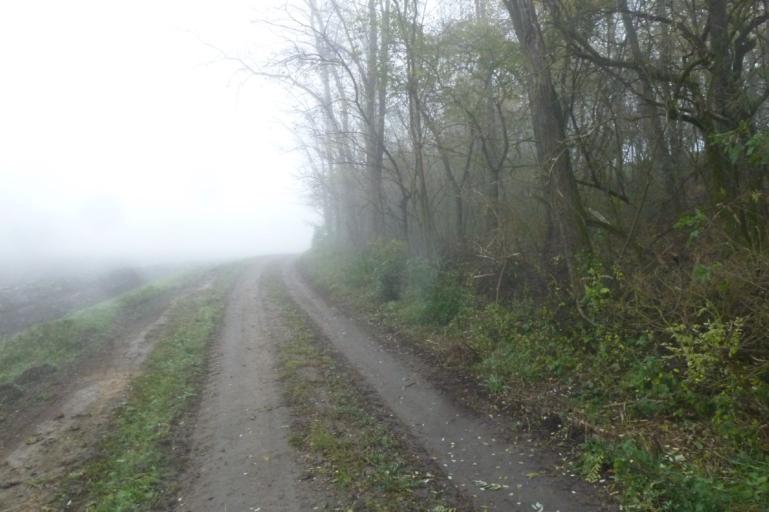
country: HU
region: Pest
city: Galgamacsa
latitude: 47.6972
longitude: 19.4031
